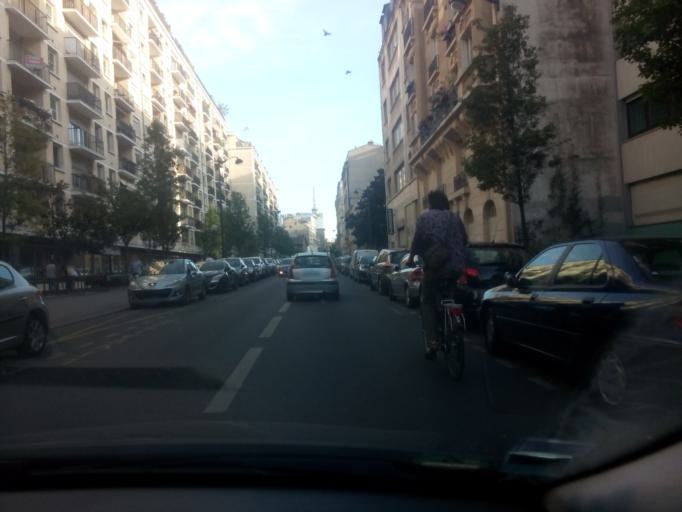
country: FR
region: Ile-de-France
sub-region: Departement du Val-de-Marne
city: Gentilly
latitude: 48.8296
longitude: 2.3463
